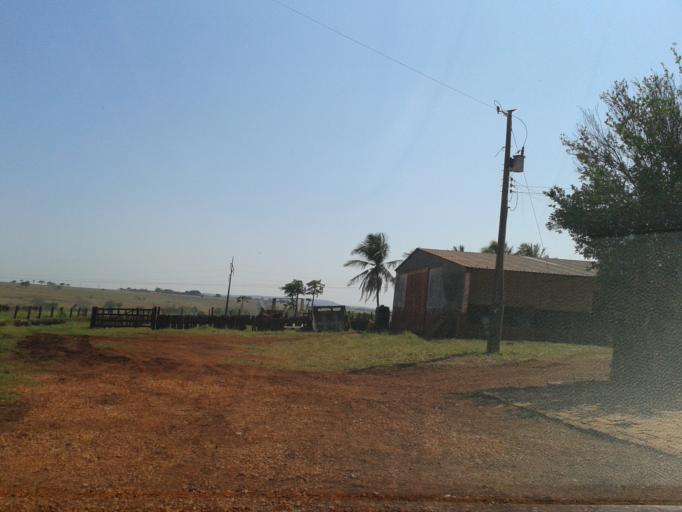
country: BR
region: Minas Gerais
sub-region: Ituiutaba
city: Ituiutaba
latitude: -18.9505
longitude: -49.4504
